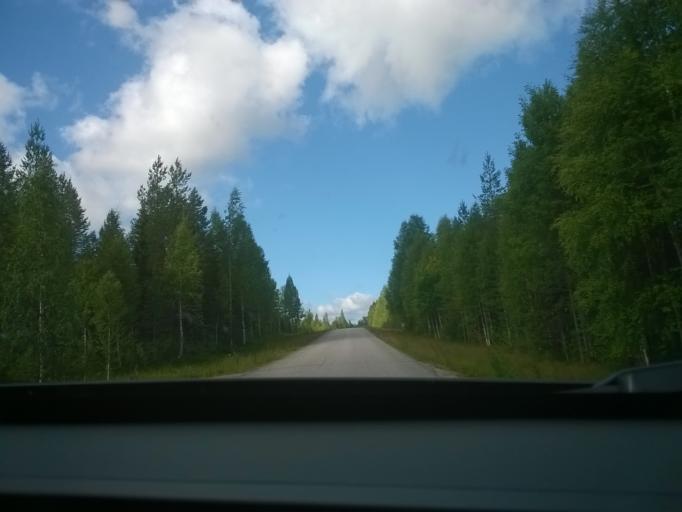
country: FI
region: Kainuu
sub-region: Kehys-Kainuu
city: Kuhmo
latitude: 64.4505
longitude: 29.6779
